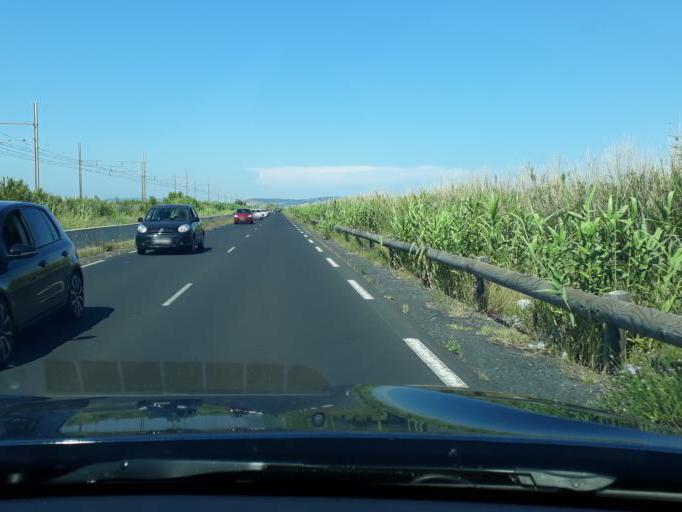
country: FR
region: Languedoc-Roussillon
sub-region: Departement de l'Herault
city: Marseillan
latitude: 43.3516
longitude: 3.5898
